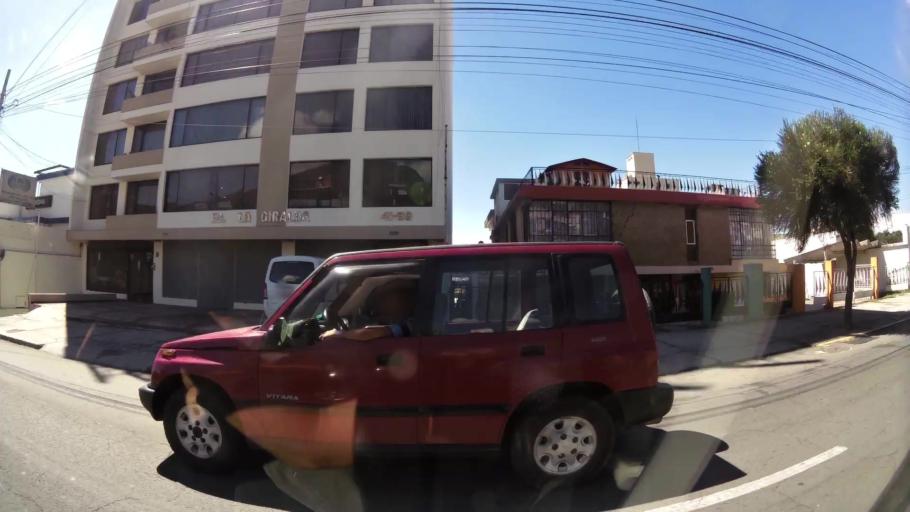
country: EC
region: Pichincha
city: Quito
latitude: -0.1805
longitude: -78.4944
